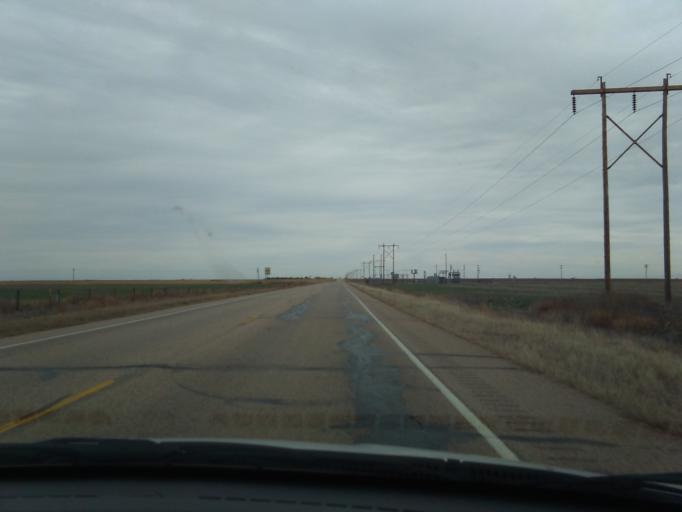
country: US
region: Colorado
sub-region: Yuma County
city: Yuma
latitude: 40.1489
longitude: -102.8938
